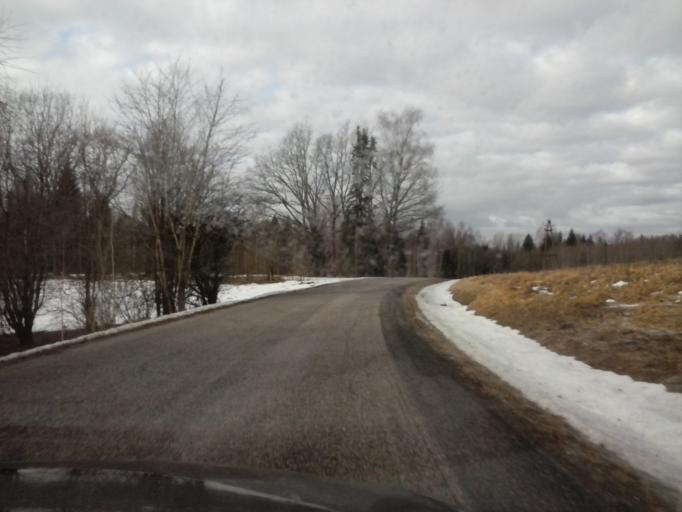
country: EE
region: Tartu
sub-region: Elva linn
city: Elva
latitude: 58.0182
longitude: 26.3212
